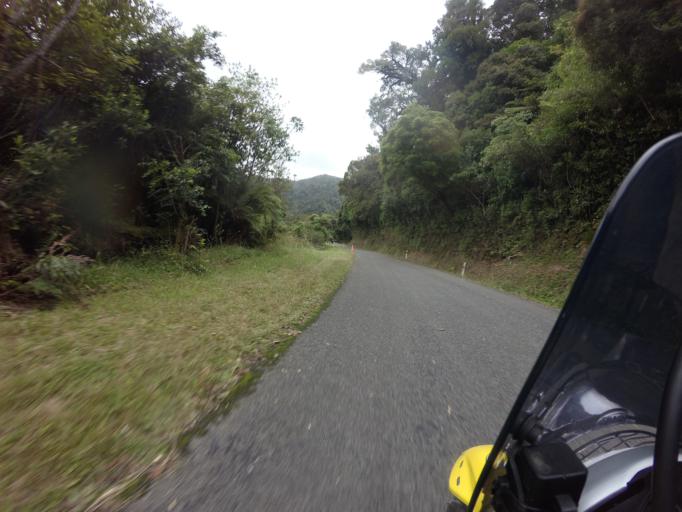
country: NZ
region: Hawke's Bay
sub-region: Wairoa District
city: Wairoa
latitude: -38.7126
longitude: 177.0674
